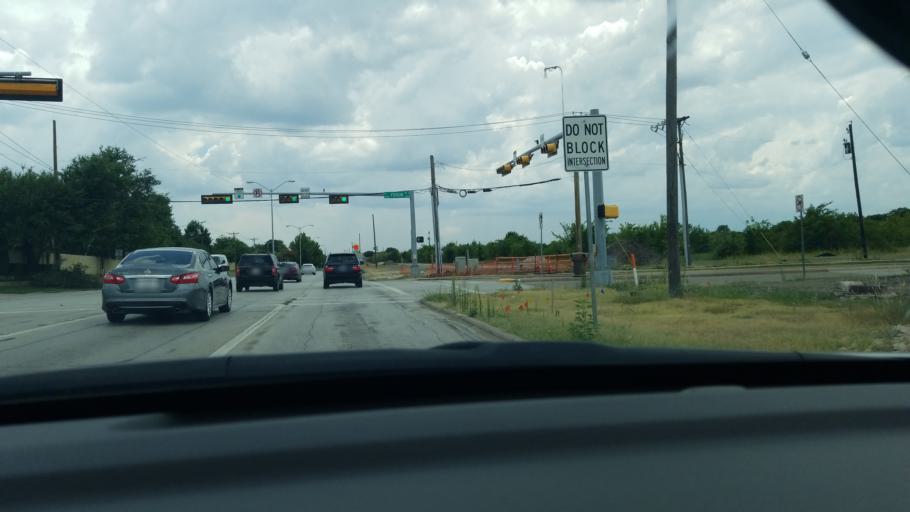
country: US
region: Texas
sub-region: Dallas County
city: Grand Prairie
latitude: 32.6844
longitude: -97.0443
